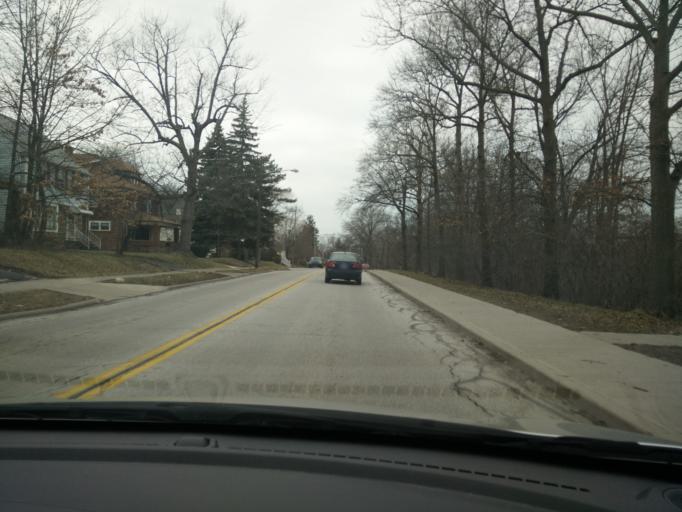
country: US
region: Ohio
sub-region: Cuyahoga County
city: Cleveland Heights
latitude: 41.5051
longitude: -81.5569
